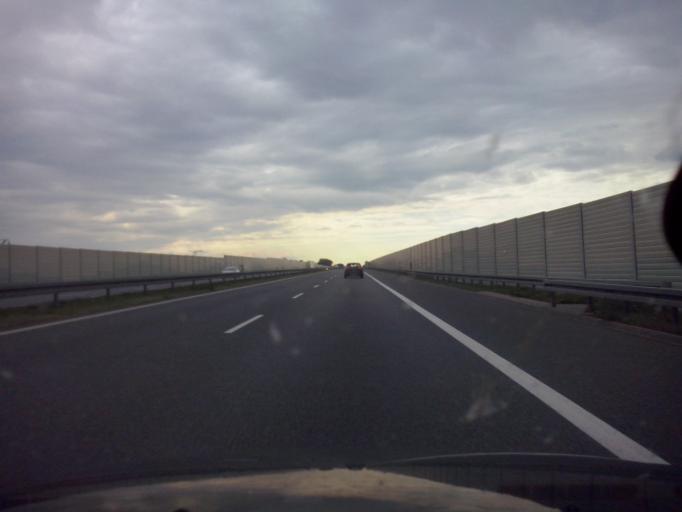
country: PL
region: Lesser Poland Voivodeship
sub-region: Powiat wielicki
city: Wegrzce Wielkie
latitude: 50.0185
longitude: 20.1179
